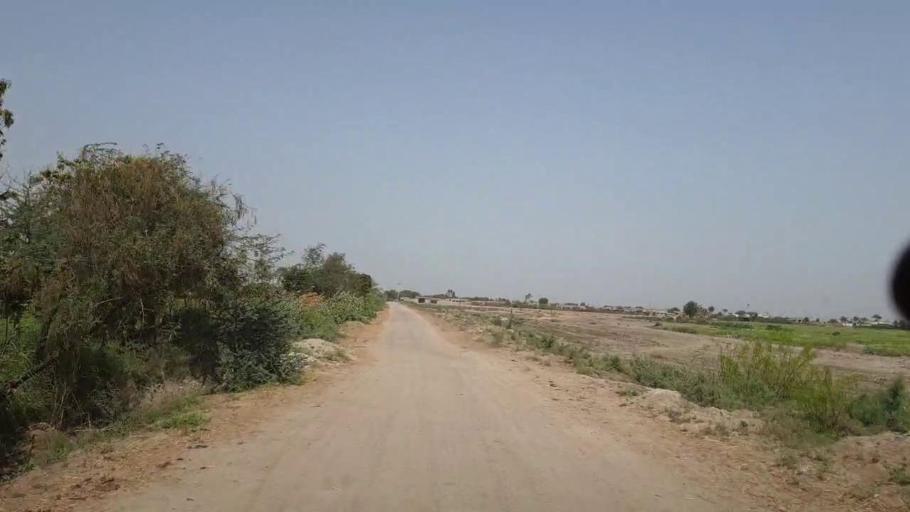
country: PK
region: Sindh
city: Matli
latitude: 25.0765
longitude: 68.6894
